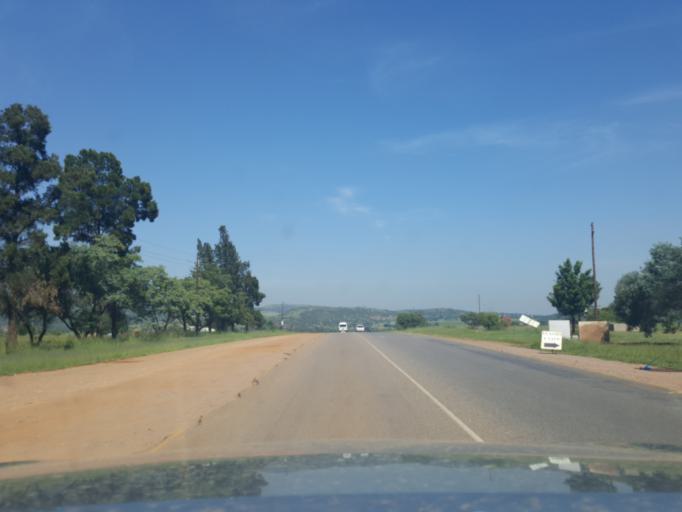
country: ZA
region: Gauteng
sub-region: City of Tshwane Metropolitan Municipality
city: Cullinan
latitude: -25.6792
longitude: 28.3777
